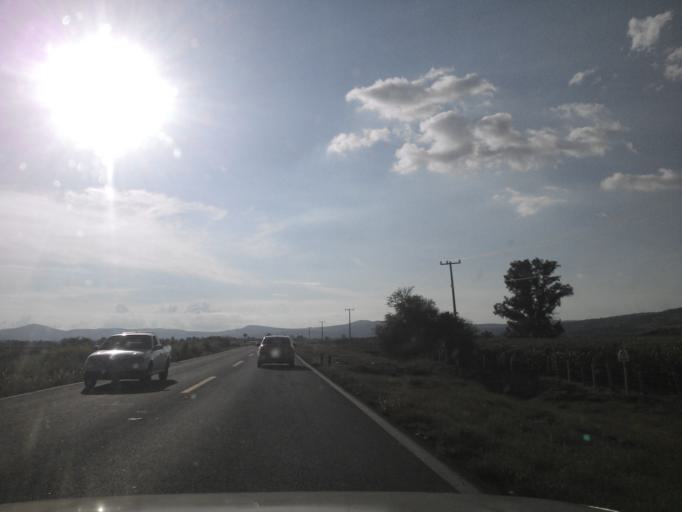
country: MX
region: Jalisco
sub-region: Tototlan
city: Nuevo Refugio de Afuera (Nuevo Refugio)
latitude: 20.5531
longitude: -102.6885
